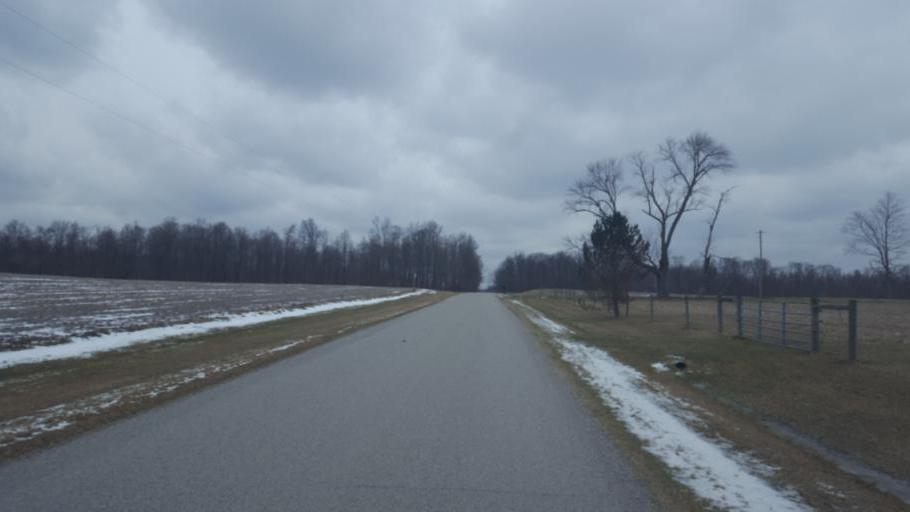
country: US
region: Ohio
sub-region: Crawford County
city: Galion
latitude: 40.6562
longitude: -82.7088
